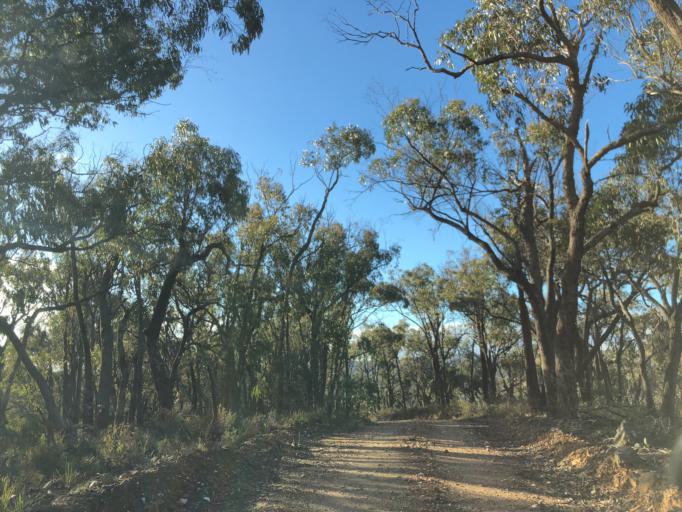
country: AU
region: Victoria
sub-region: Mount Alexander
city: Castlemaine
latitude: -37.2326
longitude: 144.2693
